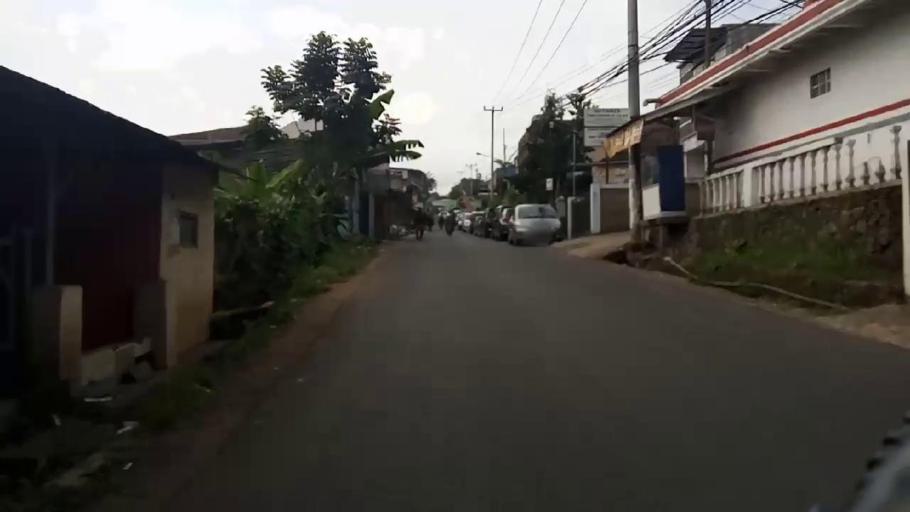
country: ID
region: West Java
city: Cimahi
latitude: -6.8562
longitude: 107.5790
